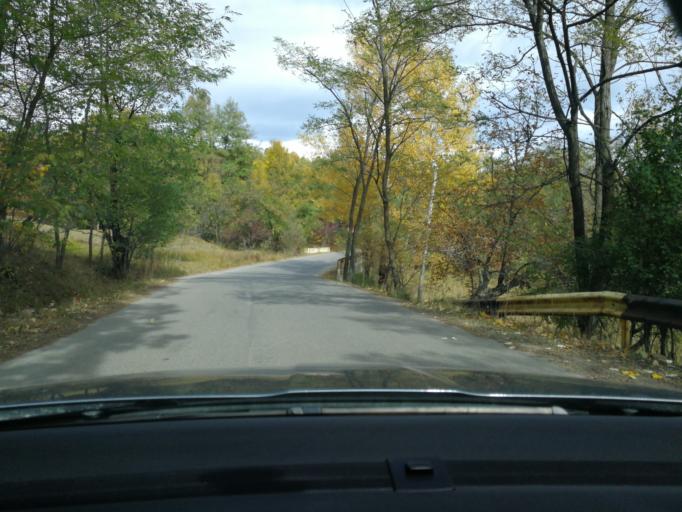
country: RO
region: Prahova
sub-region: Comuna Brebu
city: Pietriceaua
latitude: 45.2050
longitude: 25.7886
